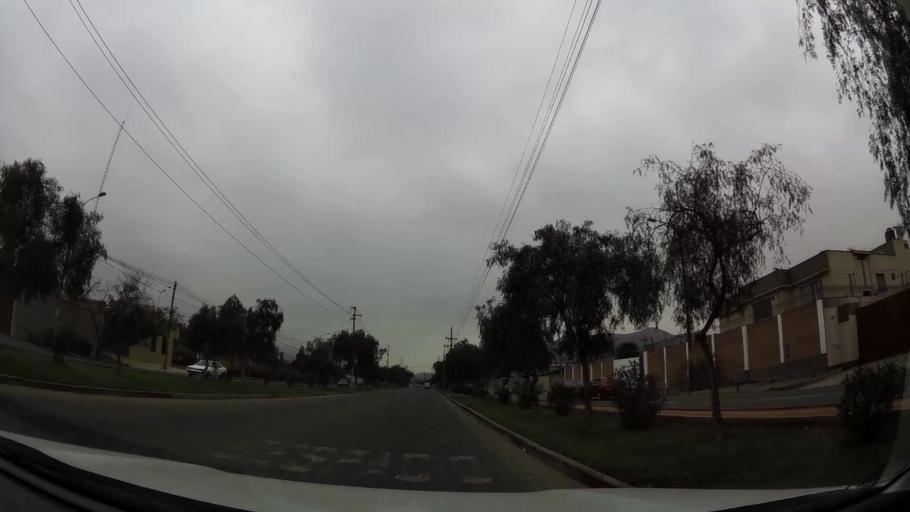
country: PE
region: Lima
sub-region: Lima
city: La Molina
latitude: -12.0862
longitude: -76.9065
